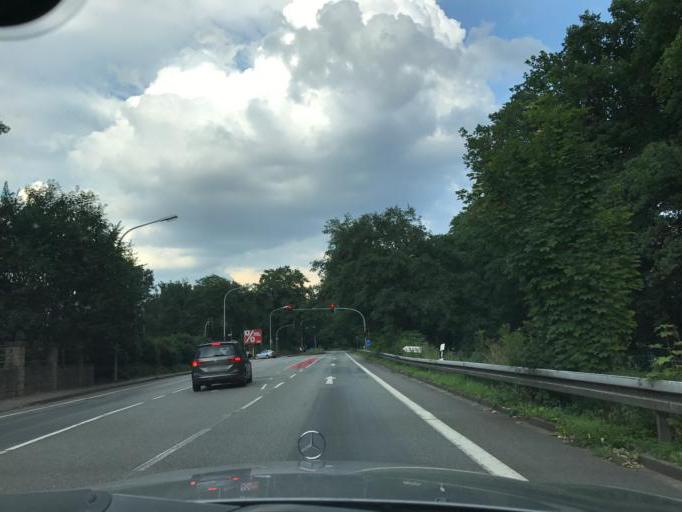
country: DE
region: Lower Saxony
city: Belm
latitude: 52.2683
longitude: 8.1110
